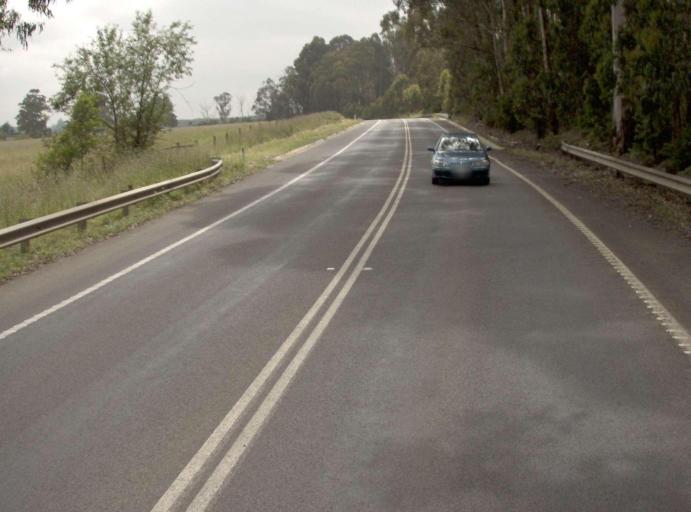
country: AU
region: Victoria
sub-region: Latrobe
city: Moe
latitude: -38.3597
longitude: 146.1863
